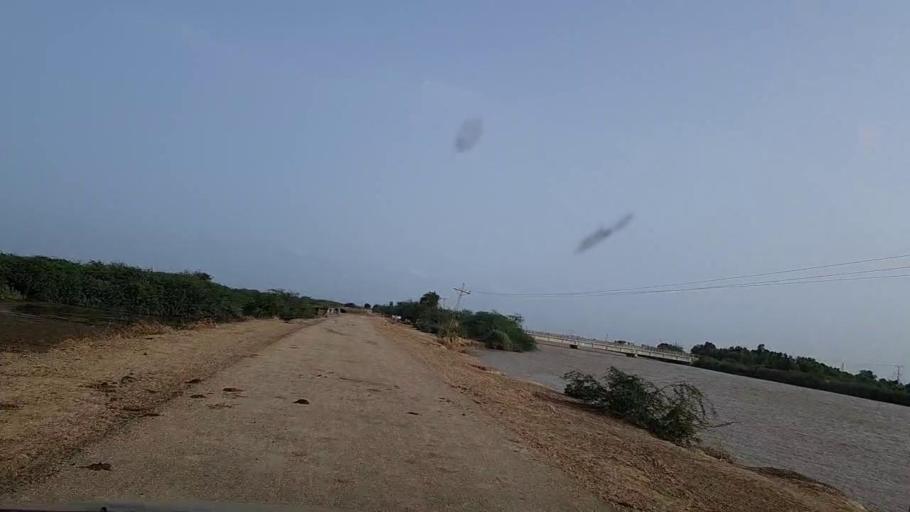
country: PK
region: Sindh
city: Kotri
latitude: 25.1894
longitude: 68.2591
